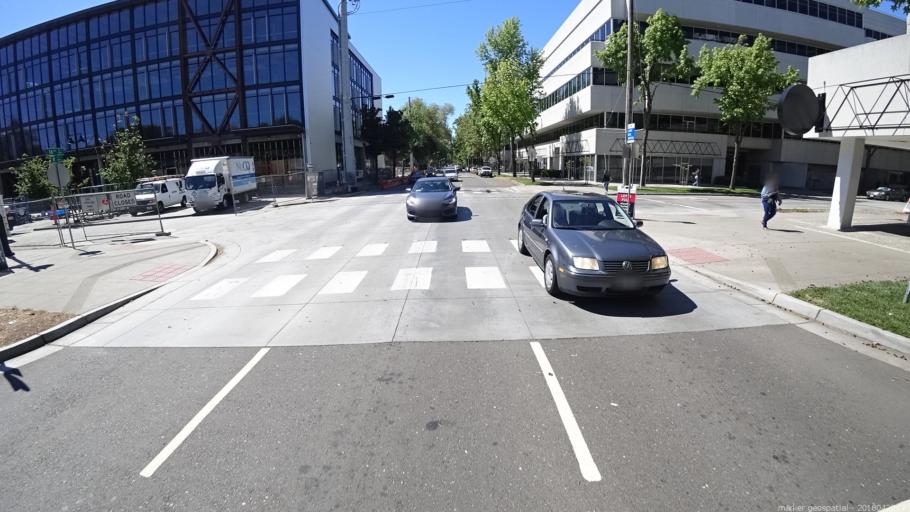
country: US
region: California
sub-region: Sacramento County
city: Sacramento
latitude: 38.5694
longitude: -121.4891
